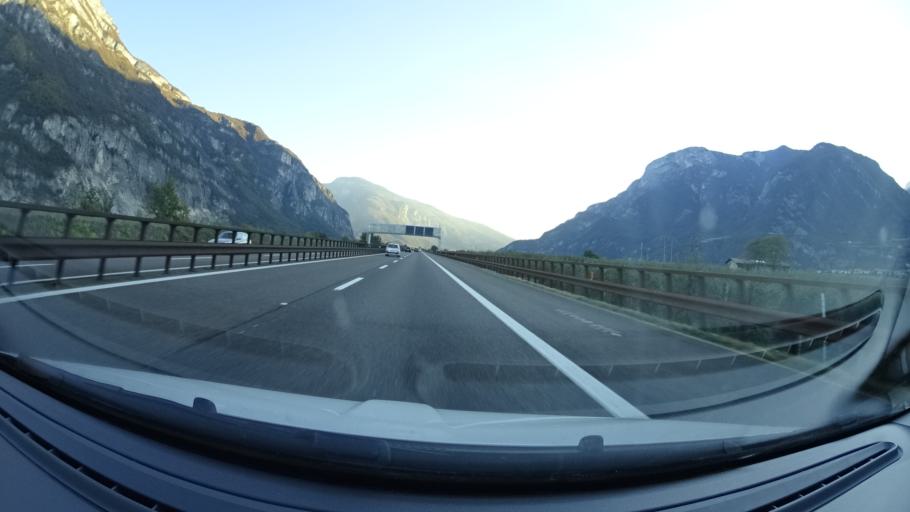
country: IT
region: Trentino-Alto Adige
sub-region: Provincia di Trento
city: Aldeno
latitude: 45.9789
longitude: 11.1081
